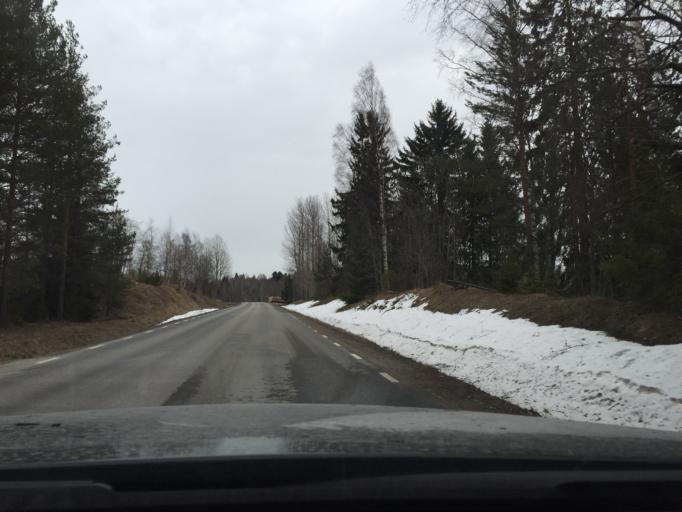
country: SE
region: Gaevleborg
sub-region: Sandvikens Kommun
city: Jarbo
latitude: 60.7618
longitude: 16.5254
